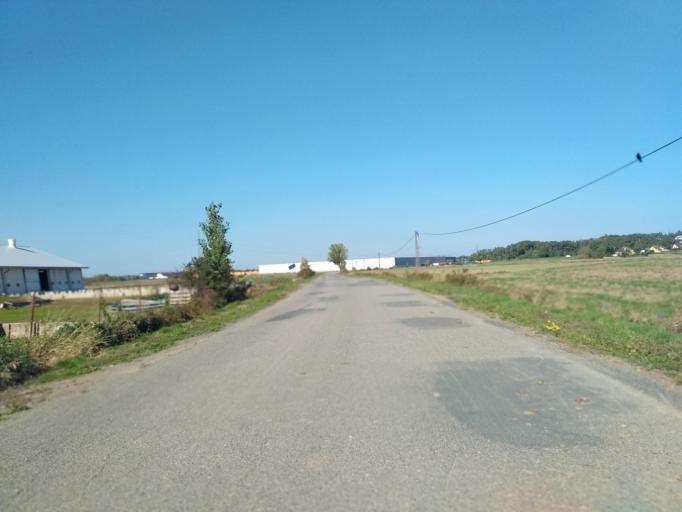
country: PL
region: Subcarpathian Voivodeship
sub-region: Powiat debicki
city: Pilzno
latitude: 49.9791
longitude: 21.3256
